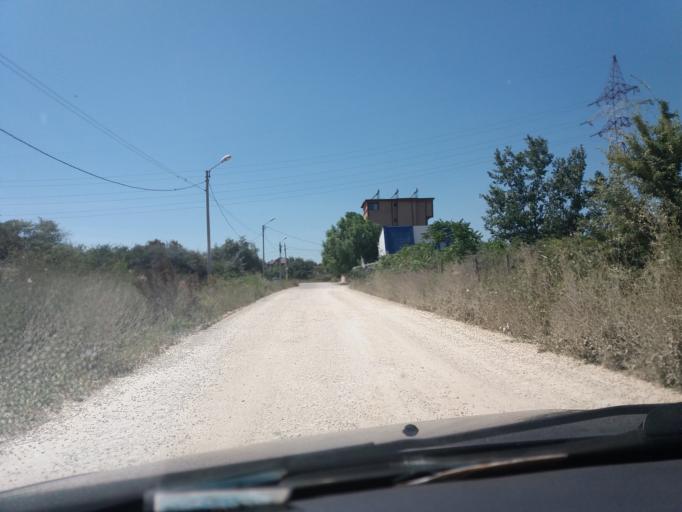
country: RO
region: Constanta
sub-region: Comuna Navodari
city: Navodari
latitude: 44.3214
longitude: 28.6301
